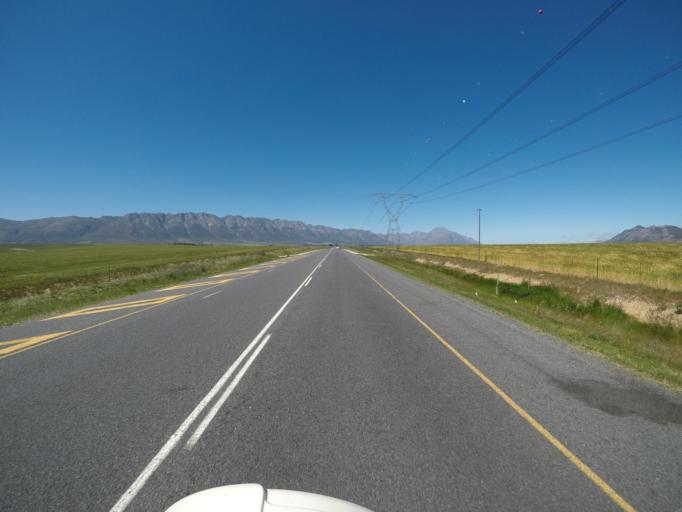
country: ZA
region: Western Cape
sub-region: Cape Winelands District Municipality
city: Ceres
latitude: -33.3104
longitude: 19.1178
